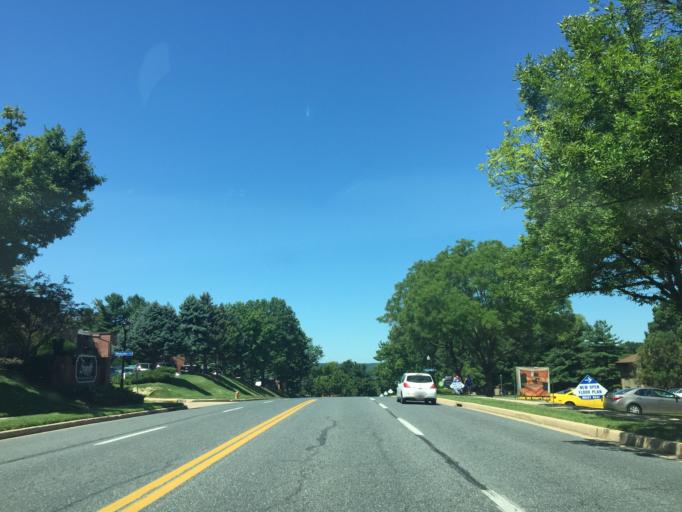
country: US
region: Maryland
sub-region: Baltimore County
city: Cockeysville
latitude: 39.4706
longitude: -76.6164
